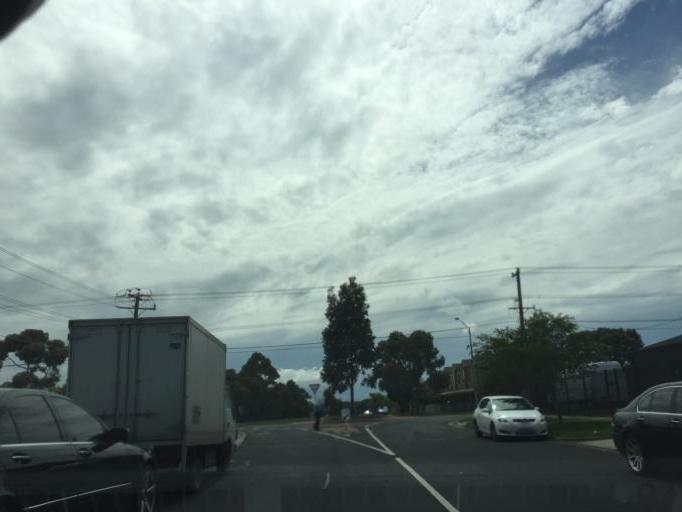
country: AU
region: Victoria
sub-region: Maribyrnong
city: Braybrook
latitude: -37.7781
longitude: 144.8524
